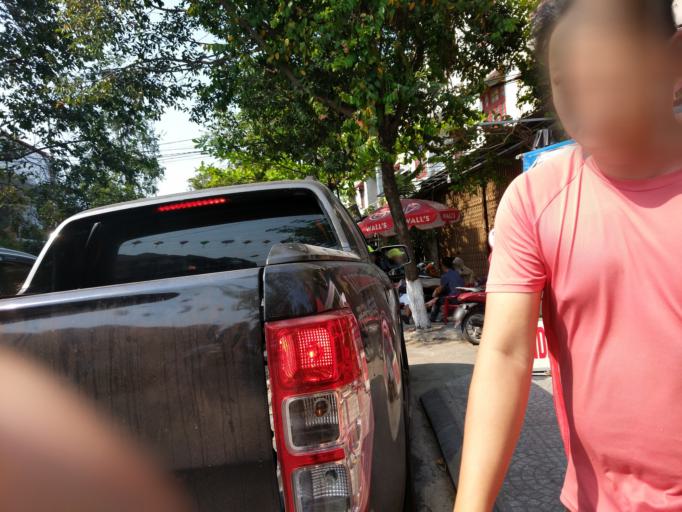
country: VN
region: Quang Nam
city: Hoi An
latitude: 15.8806
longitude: 108.3268
